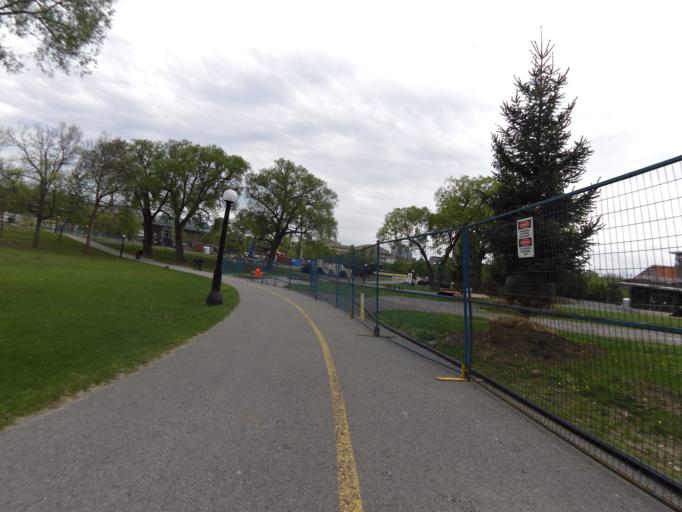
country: CA
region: Ontario
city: Ottawa
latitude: 45.4340
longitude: -75.7080
